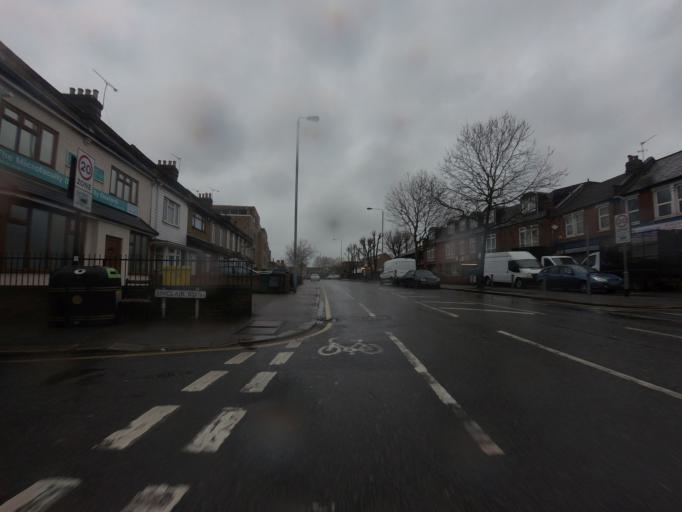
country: GB
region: England
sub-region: Greater London
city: Walthamstow
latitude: 51.6117
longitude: -0.0180
